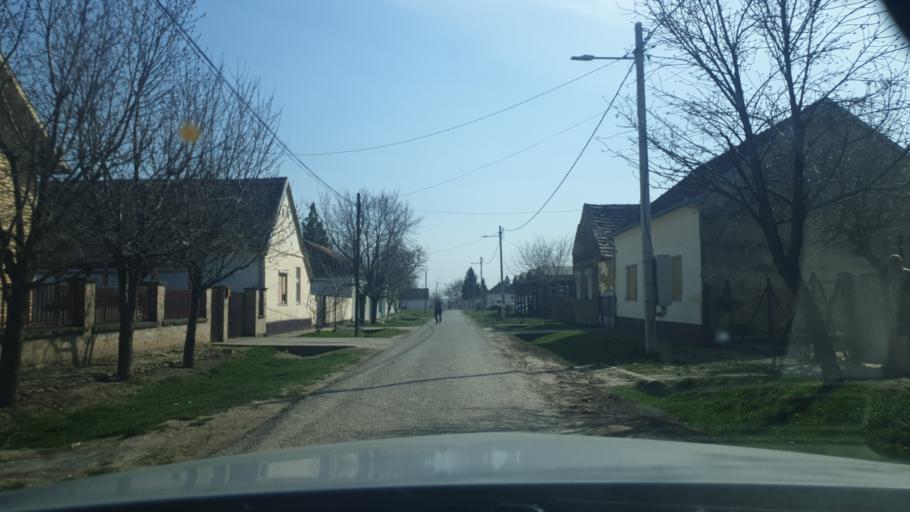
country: RS
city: Putinci
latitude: 45.0412
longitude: 19.9398
